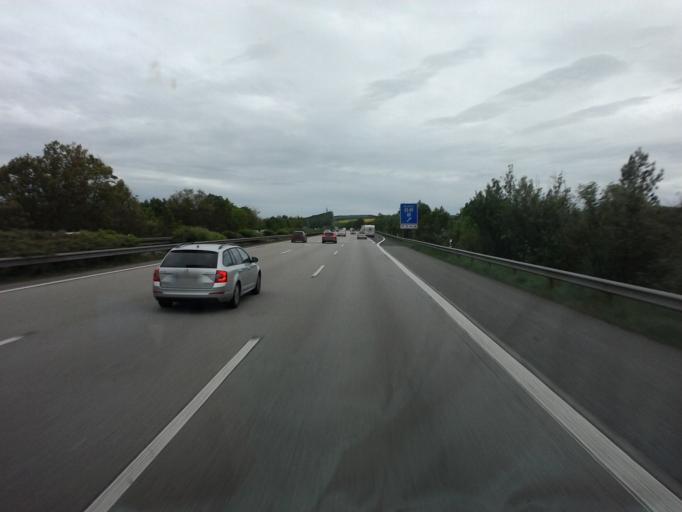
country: DE
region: Rheinland-Pfalz
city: Niederzissen
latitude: 50.4461
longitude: 7.2277
